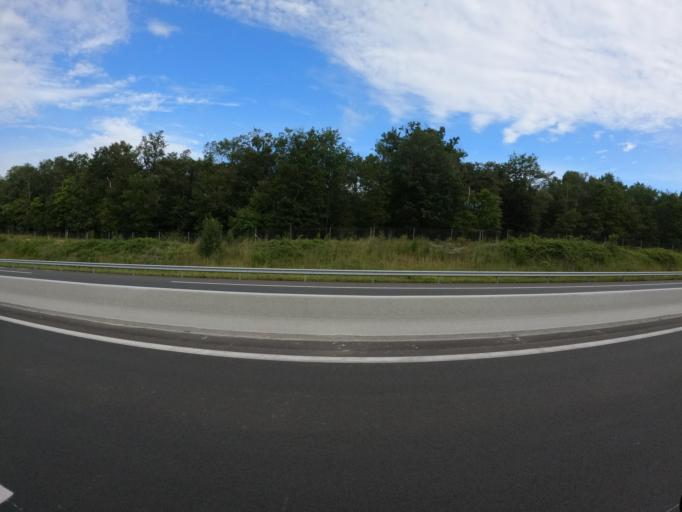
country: FR
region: Centre
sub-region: Departement d'Indre-et-Loire
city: Langeais
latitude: 47.3400
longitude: 0.3533
